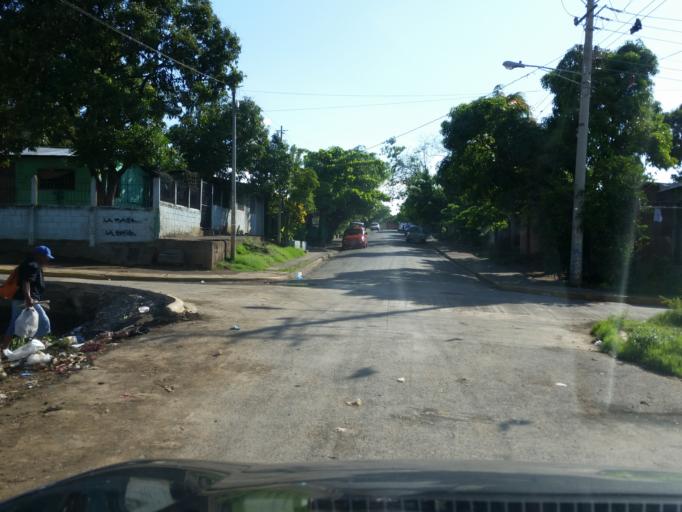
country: NI
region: Managua
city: Managua
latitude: 12.1111
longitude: -86.2256
